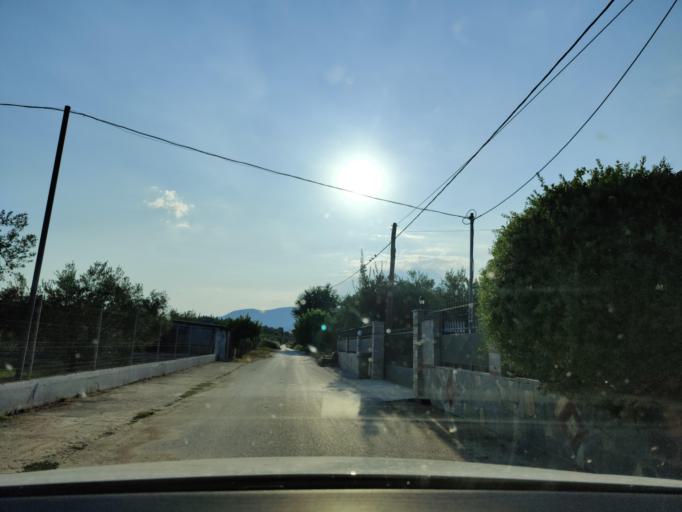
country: GR
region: East Macedonia and Thrace
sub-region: Nomos Kavalas
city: Nea Peramos
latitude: 40.8298
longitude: 24.3023
